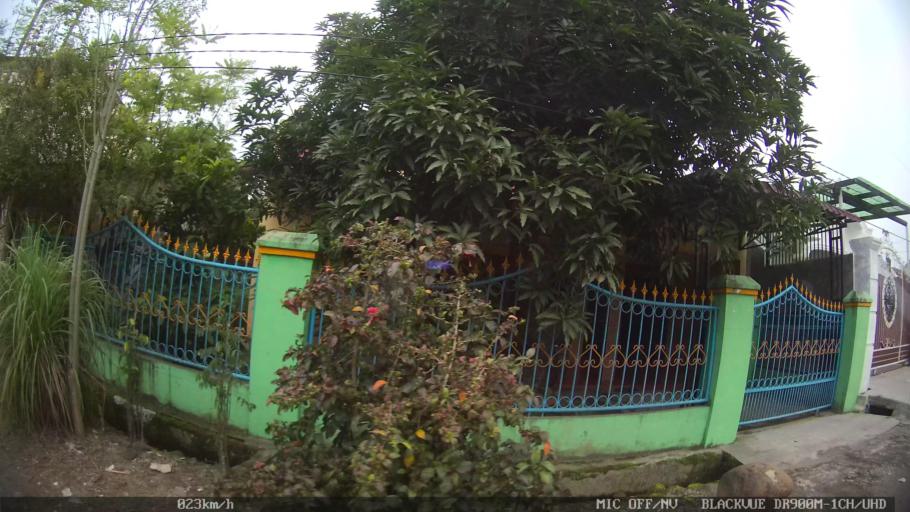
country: ID
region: North Sumatra
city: Medan
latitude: 3.5781
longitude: 98.7323
